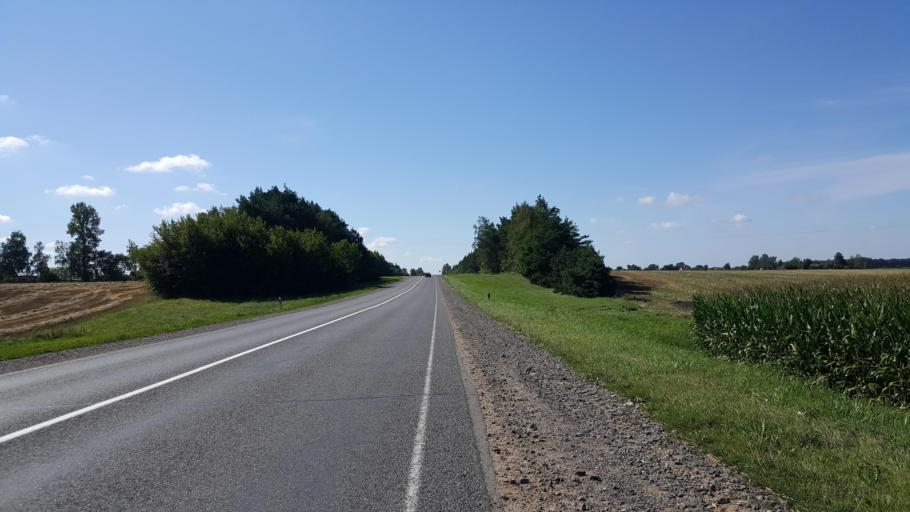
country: BY
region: Brest
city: Kamyanyets
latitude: 52.3394
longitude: 23.7808
